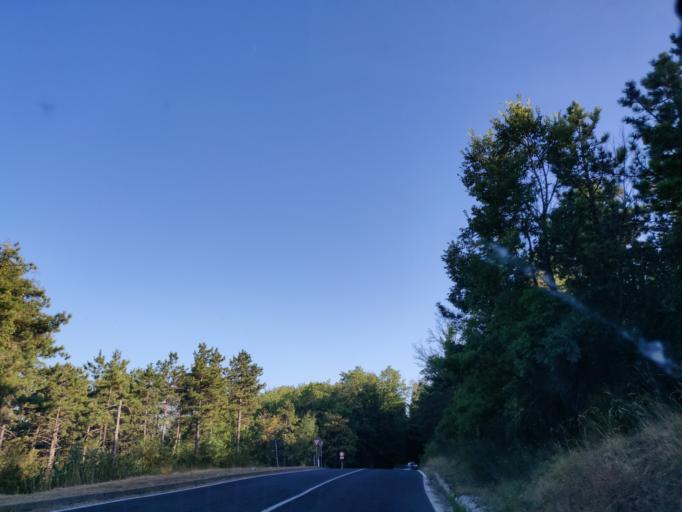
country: IT
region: Tuscany
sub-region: Provincia di Siena
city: Piancastagnaio
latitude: 42.8607
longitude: 11.6822
